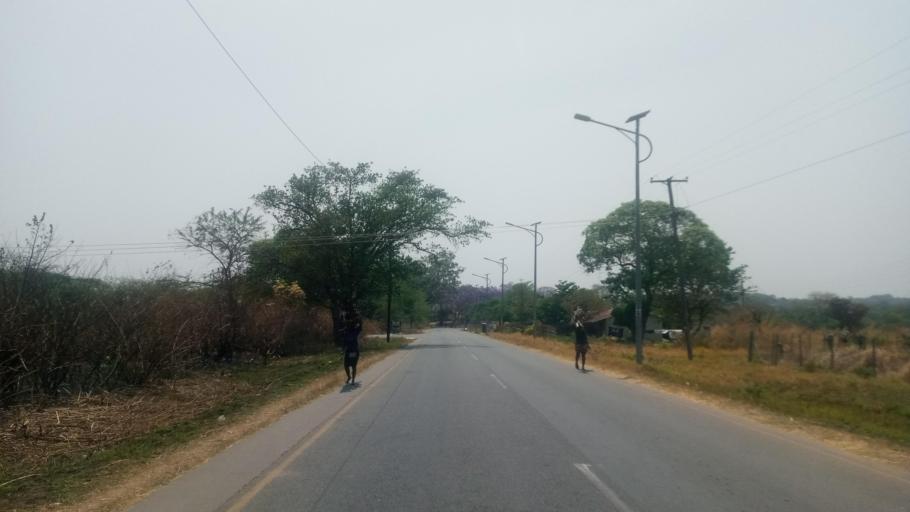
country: ZM
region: Lusaka
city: Lusaka
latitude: -15.4565
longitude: 28.4394
